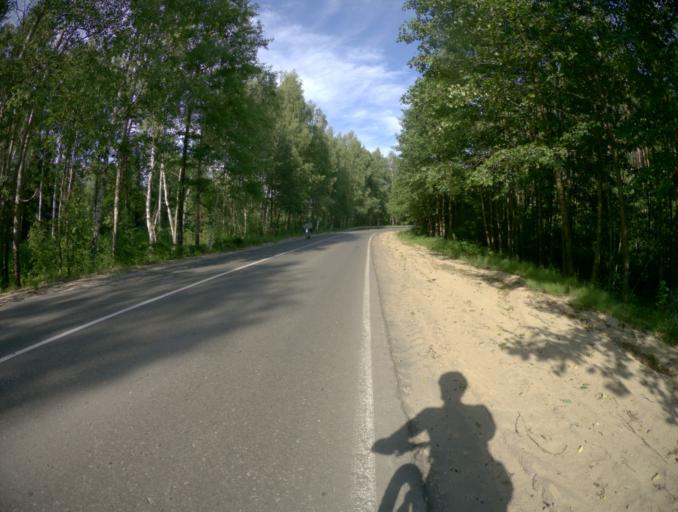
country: RU
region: Nizjnij Novgorod
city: Mulino
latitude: 56.2887
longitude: 42.8067
